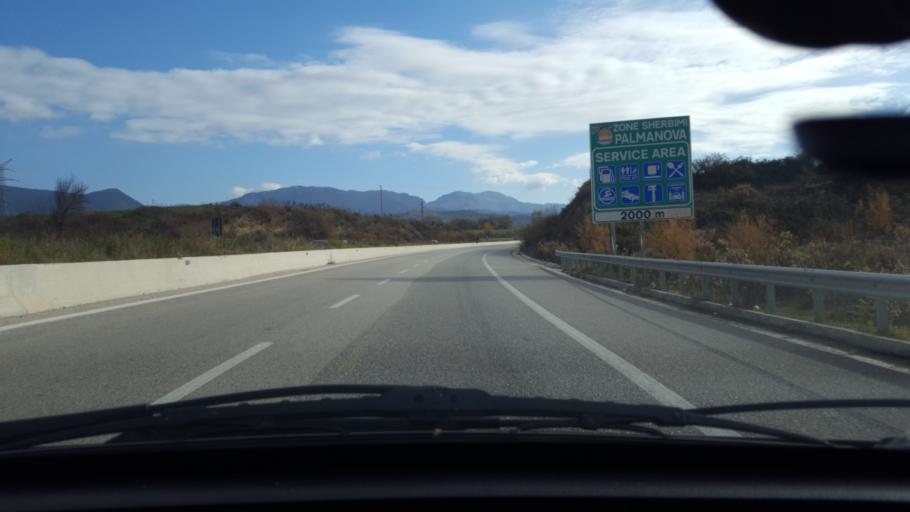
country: AL
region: Tirane
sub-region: Rrethi i Tiranes
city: Berzhite
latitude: 41.2606
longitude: 19.8857
